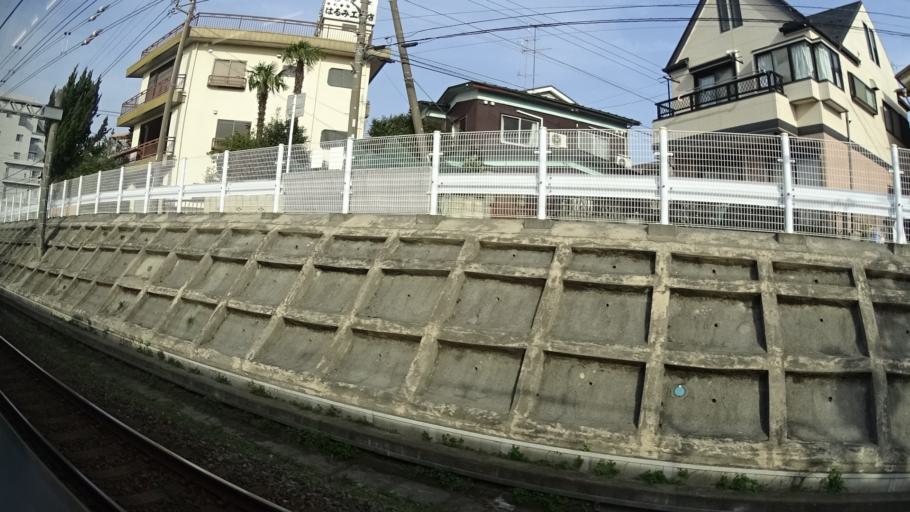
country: JP
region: Kanagawa
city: Minami-rinkan
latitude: 35.4701
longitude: 139.4224
